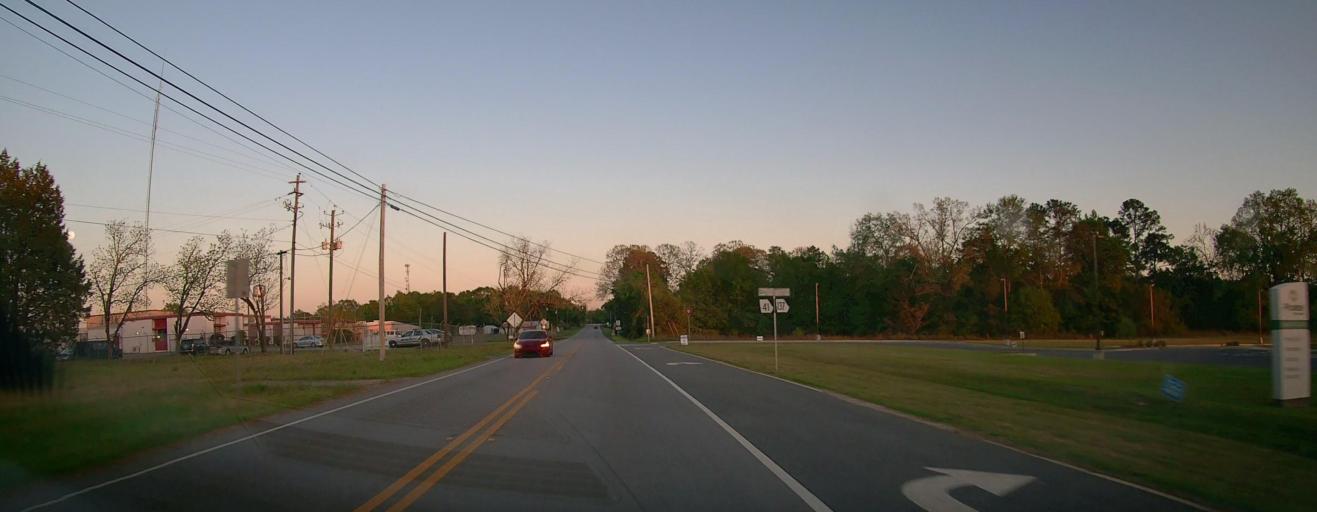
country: US
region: Georgia
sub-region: Marion County
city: Buena Vista
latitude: 32.3320
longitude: -84.5287
